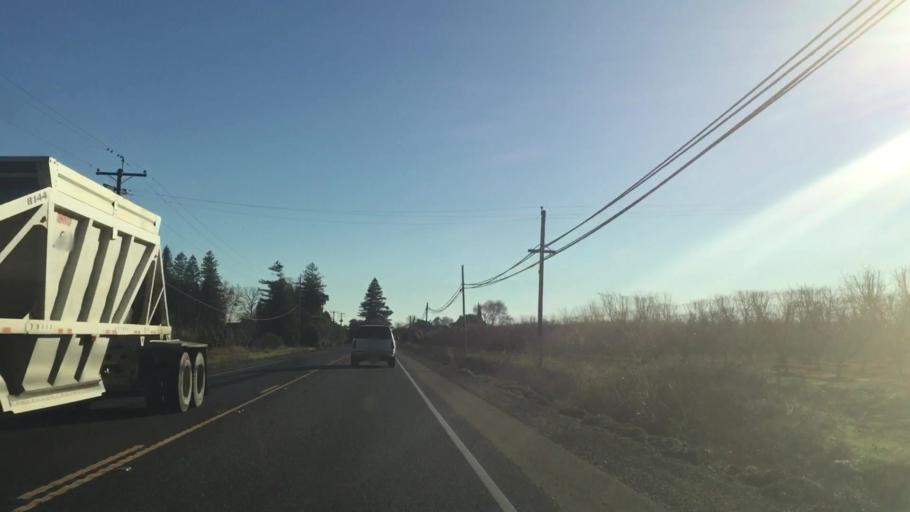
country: US
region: California
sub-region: Yuba County
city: Marysville
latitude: 39.1934
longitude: -121.5949
